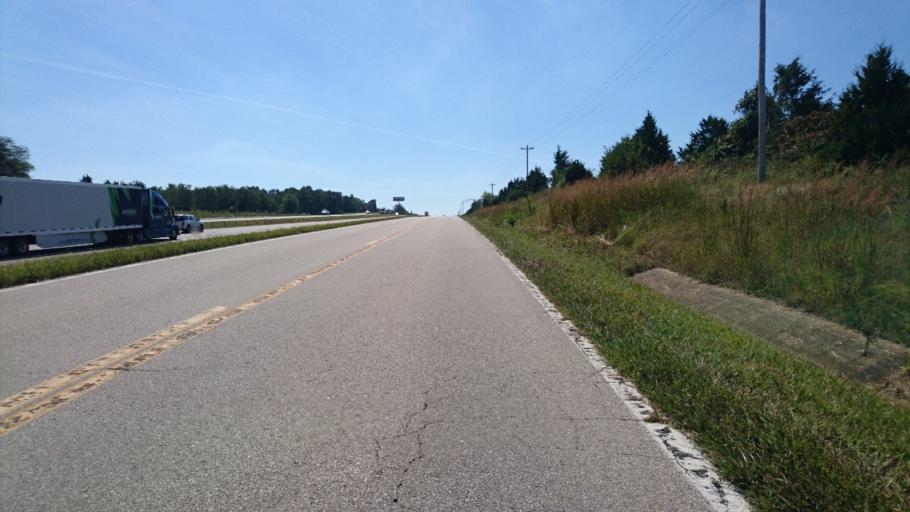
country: US
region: Missouri
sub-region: Franklin County
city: Sullivan
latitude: 38.2480
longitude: -91.1367
